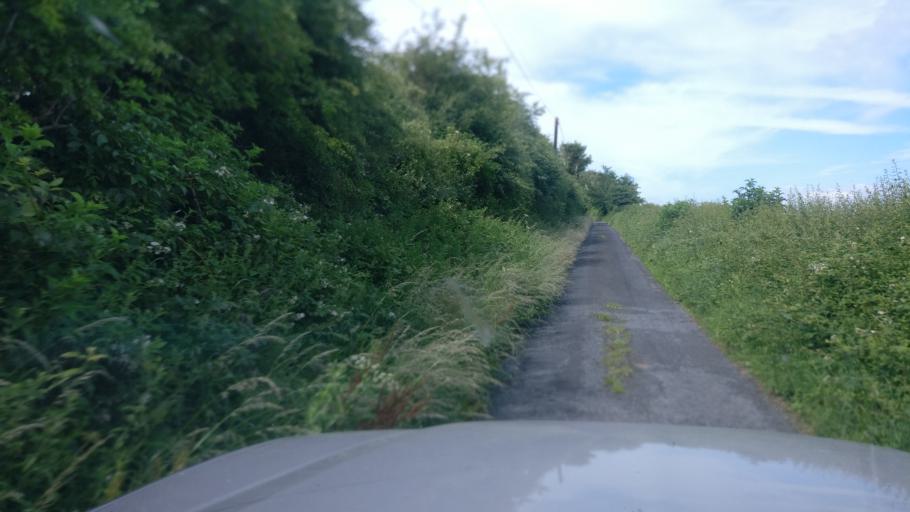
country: IE
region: Connaught
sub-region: County Galway
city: Gort
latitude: 53.0762
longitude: -8.7737
